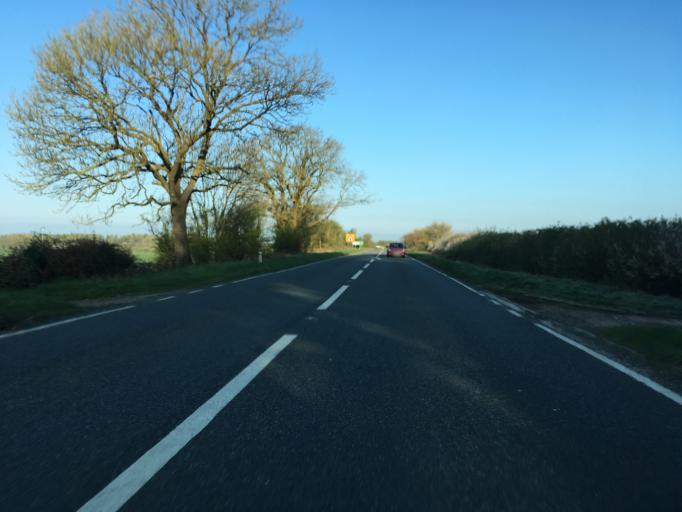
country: GB
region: England
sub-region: Gloucestershire
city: Bourton on the Water
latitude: 51.8090
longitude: -1.7192
